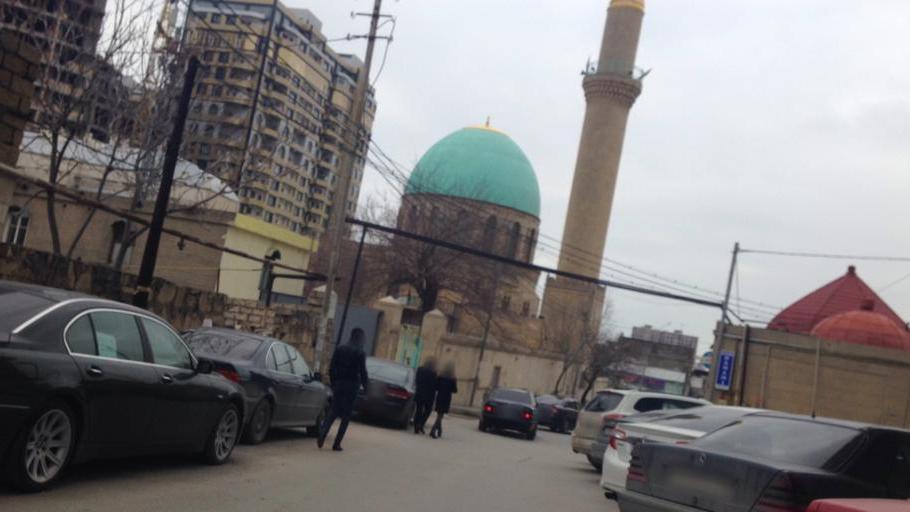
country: AZ
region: Baki
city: Badamdar
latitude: 40.3794
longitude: 49.8290
